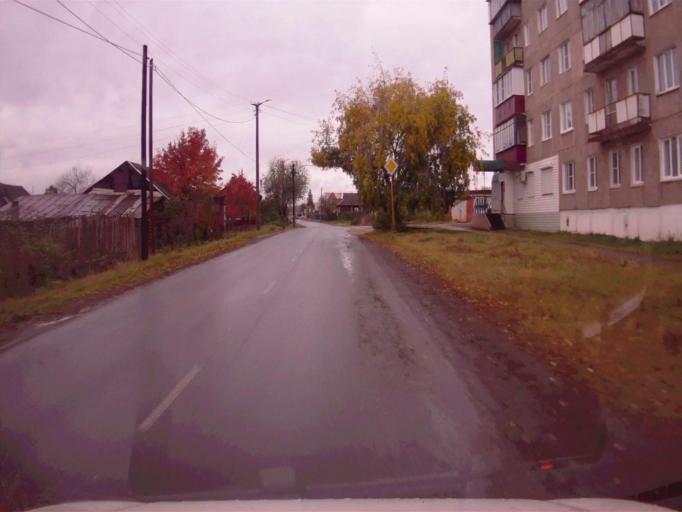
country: RU
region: Chelyabinsk
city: Verkhniy Ufaley
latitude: 56.0491
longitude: 60.2147
